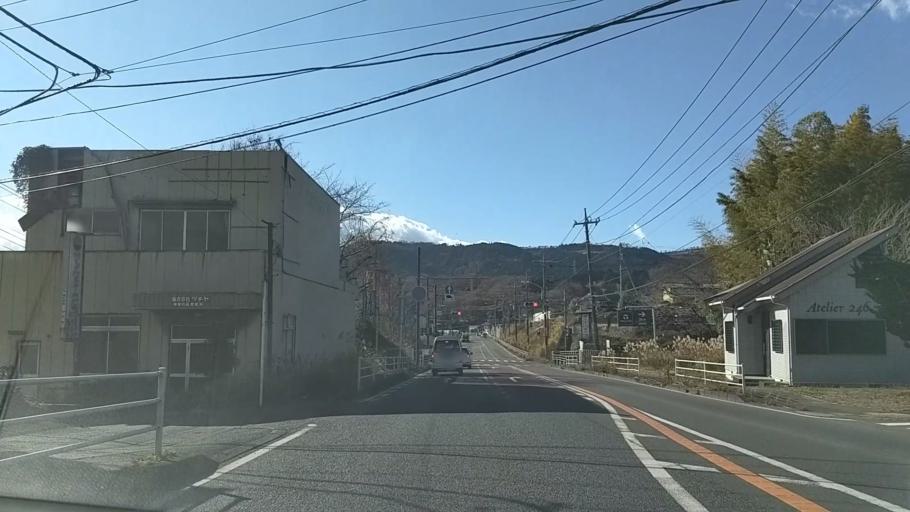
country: JP
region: Kanagawa
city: Hadano
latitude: 35.3762
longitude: 139.1669
